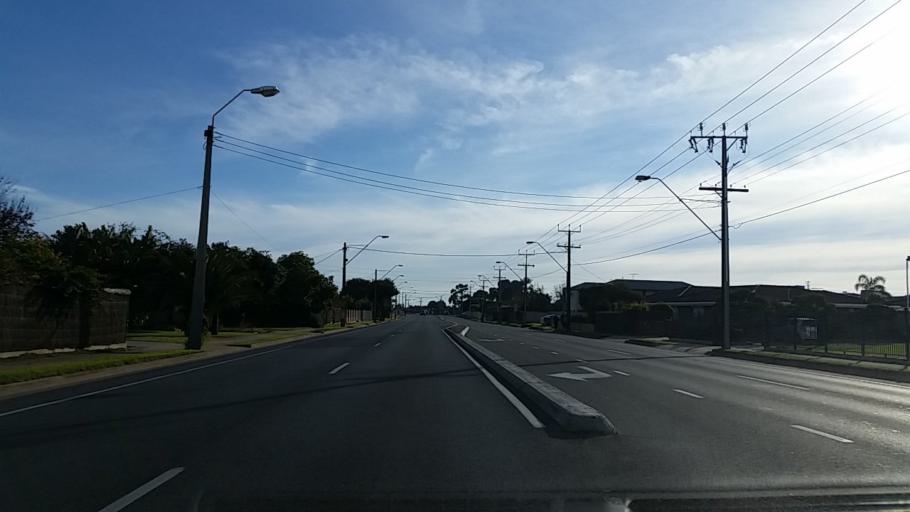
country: AU
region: South Australia
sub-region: Charles Sturt
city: Seaton
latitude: -34.9092
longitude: 138.5142
